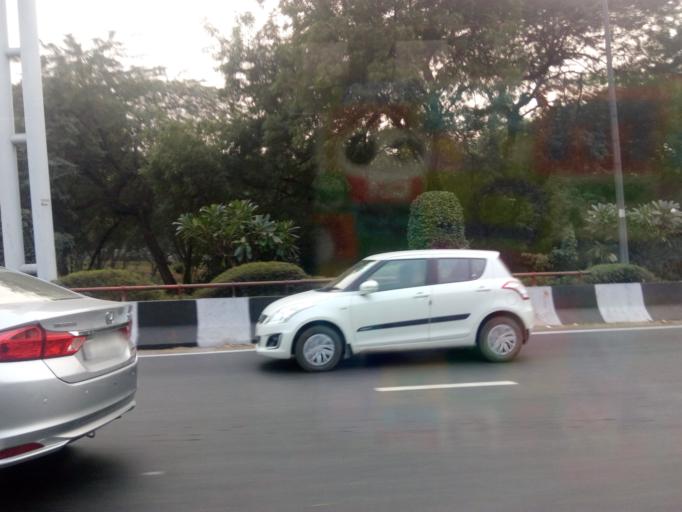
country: IN
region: NCT
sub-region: Central Delhi
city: Karol Bagh
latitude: 28.5938
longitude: 77.1680
